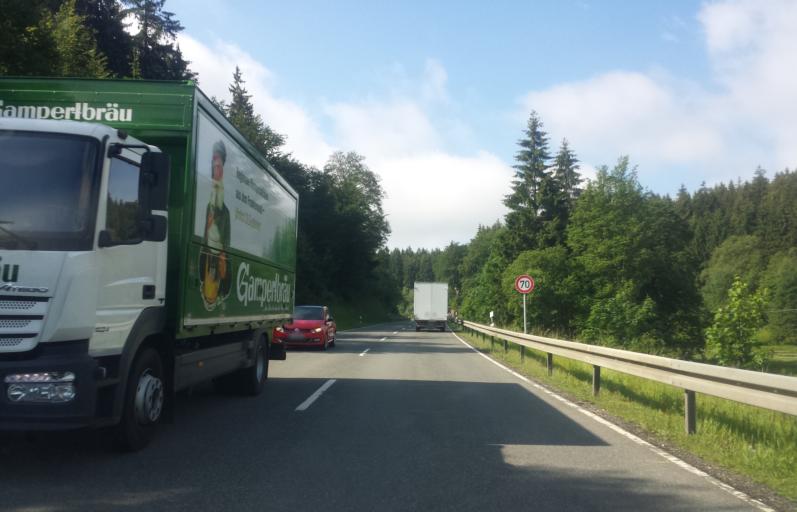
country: DE
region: Bavaria
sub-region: Upper Franconia
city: Ludwigsstadt
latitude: 50.4515
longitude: 11.3740
